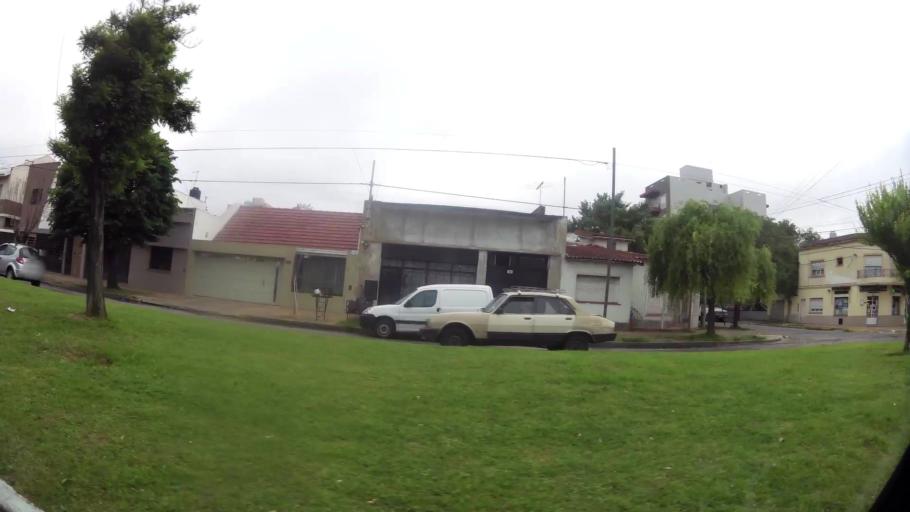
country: AR
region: Buenos Aires
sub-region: Partido de La Plata
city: La Plata
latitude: -34.9252
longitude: -57.9836
